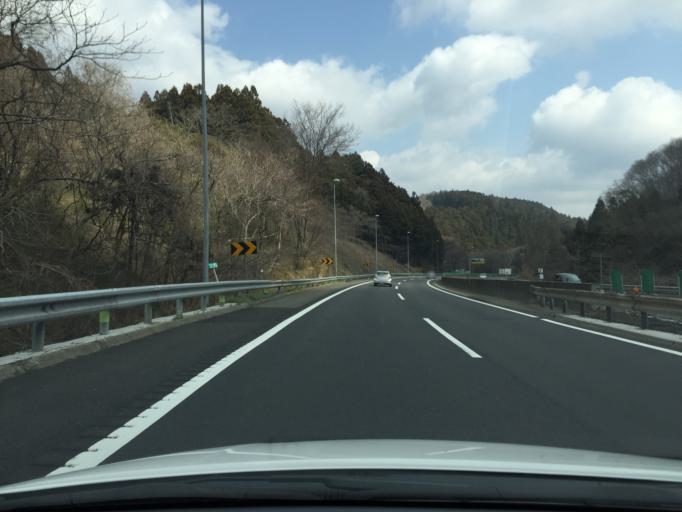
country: JP
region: Miyagi
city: Sendai
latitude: 38.1988
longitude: 140.7854
